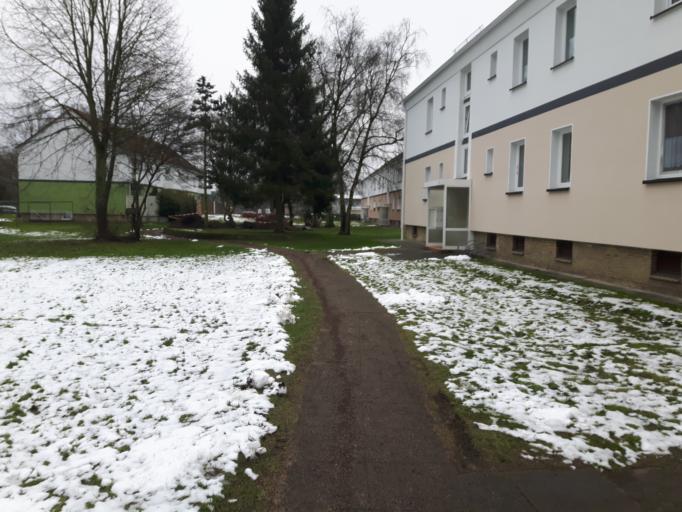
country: DE
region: Schleswig-Holstein
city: Neumunster
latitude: 54.0829
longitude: 9.9980
